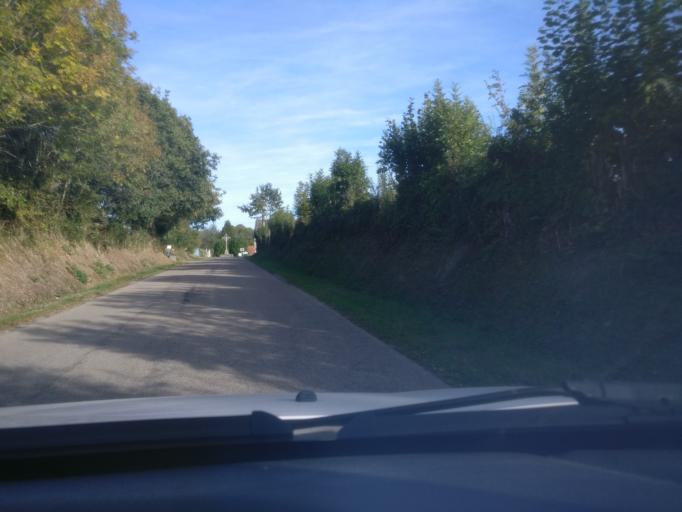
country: FR
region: Lower Normandy
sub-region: Departement de la Manche
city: Marcey-les-Greves
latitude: 48.6995
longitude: -1.4348
